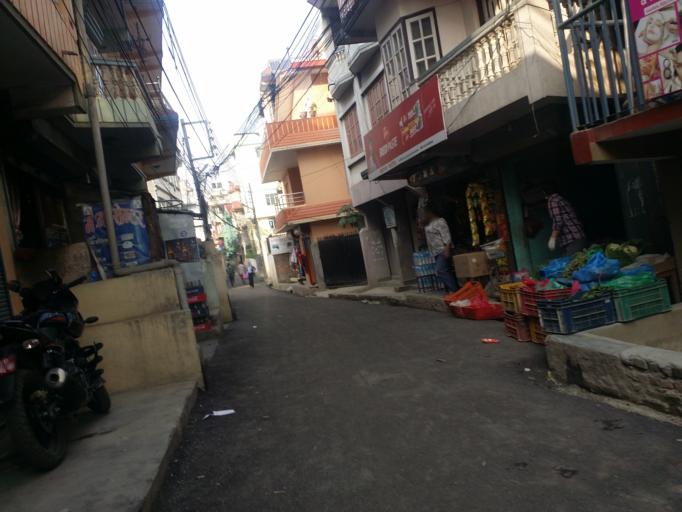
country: NP
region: Central Region
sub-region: Bagmati Zone
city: Kathmandu
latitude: 27.7022
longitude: 85.3471
